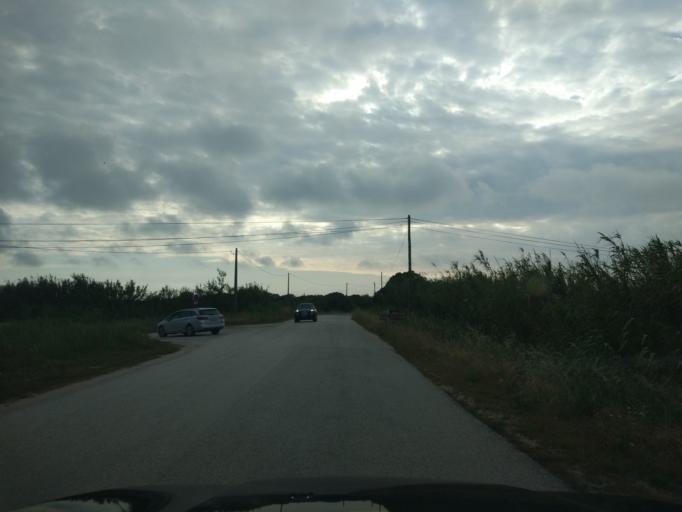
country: PT
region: Leiria
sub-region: Peniche
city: Peniche
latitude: 39.3491
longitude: -9.3630
